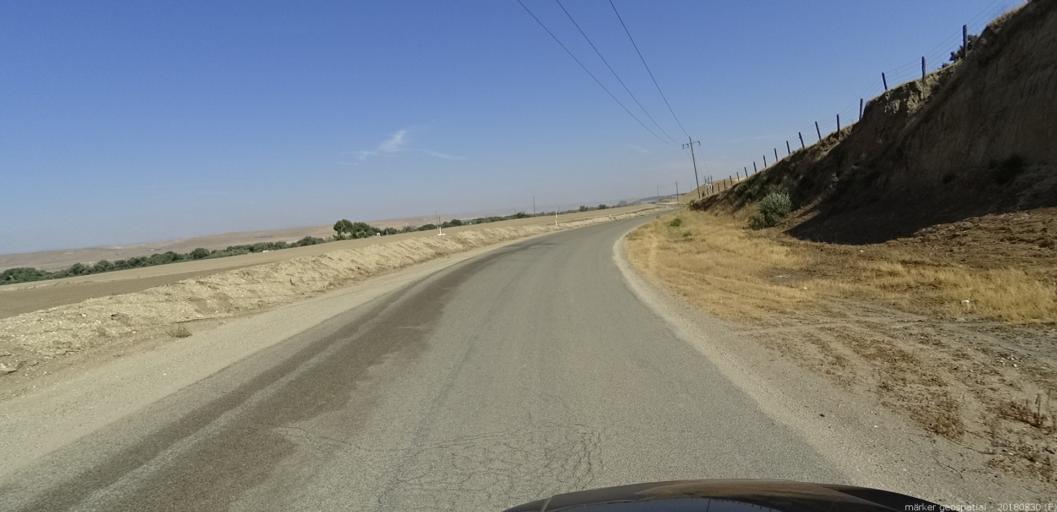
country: US
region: California
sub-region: Monterey County
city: King City
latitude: 36.1114
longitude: -121.0370
